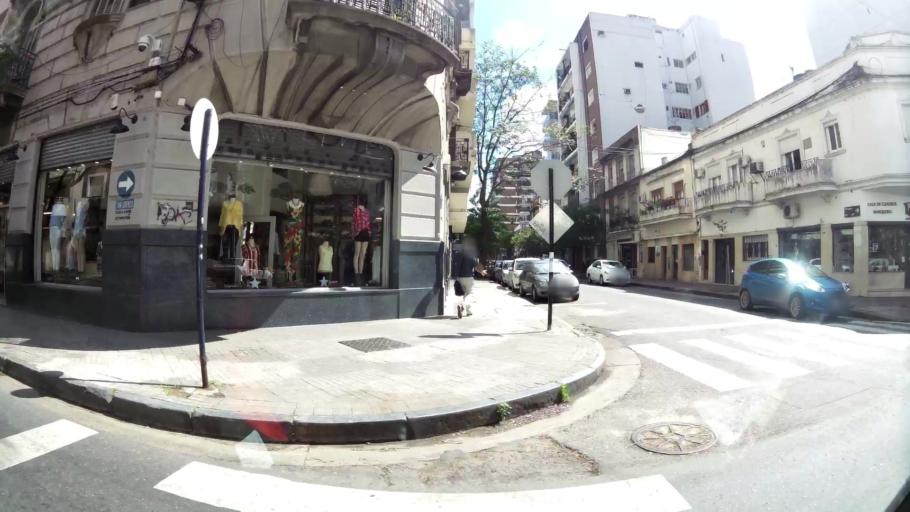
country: AR
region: Santa Fe
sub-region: Departamento de Rosario
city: Rosario
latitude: -32.9432
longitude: -60.6432
